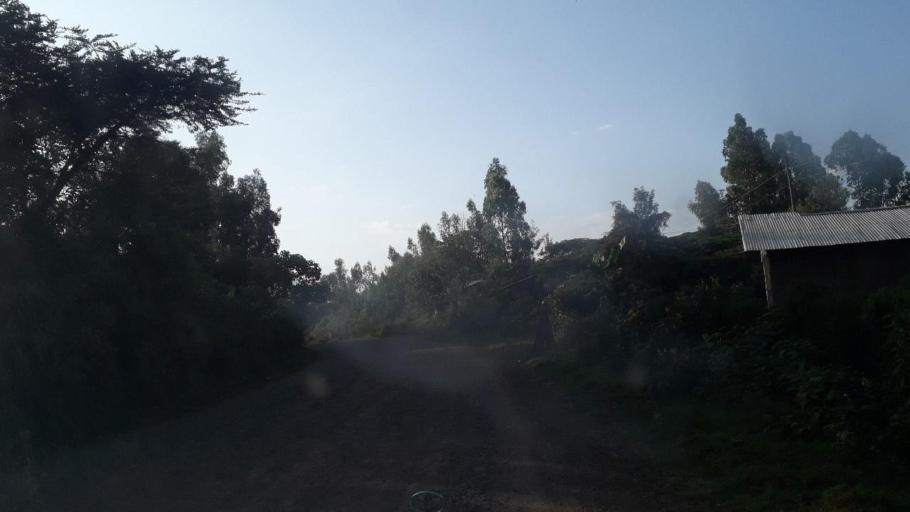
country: ET
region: Oromiya
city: Jima
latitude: 7.5916
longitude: 36.8546
